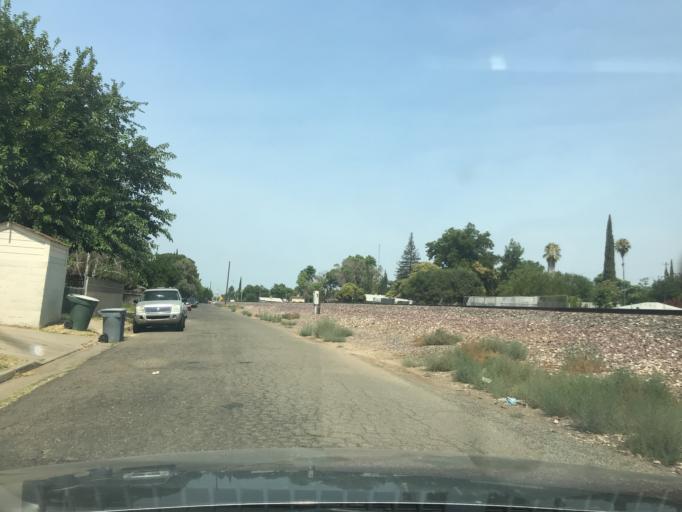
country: US
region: California
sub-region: Merced County
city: Merced
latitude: 37.3106
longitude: -120.4855
